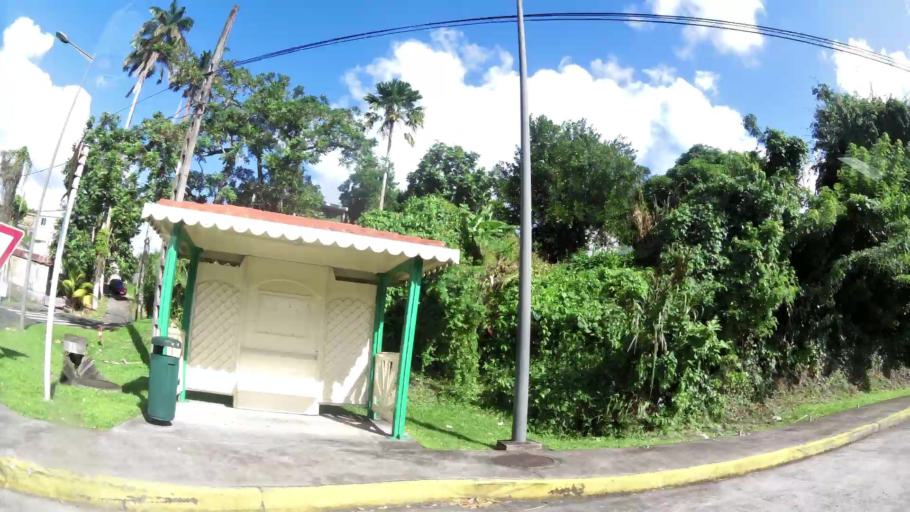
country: MQ
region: Martinique
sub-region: Martinique
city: Fort-de-France
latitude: 14.6252
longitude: -61.0724
